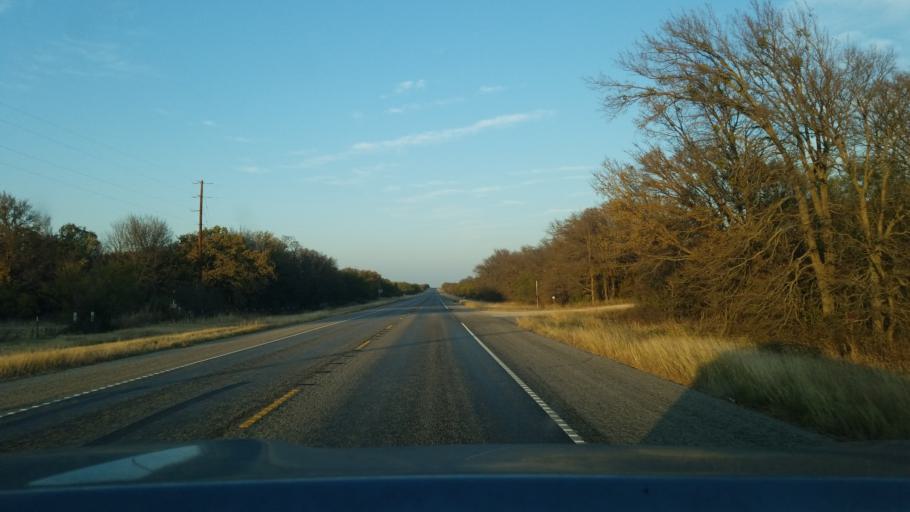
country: US
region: Texas
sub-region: Eastland County
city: Cisco
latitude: 32.4197
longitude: -98.9378
